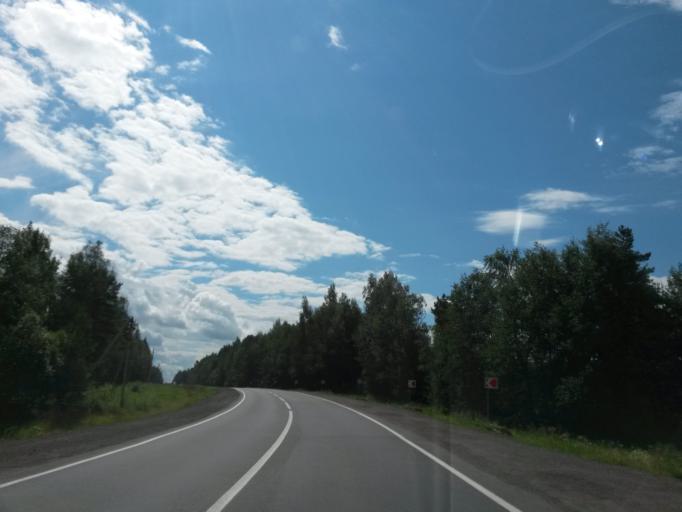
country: RU
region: Jaroslavl
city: Gavrilov-Yam
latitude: 57.2788
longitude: 39.9517
